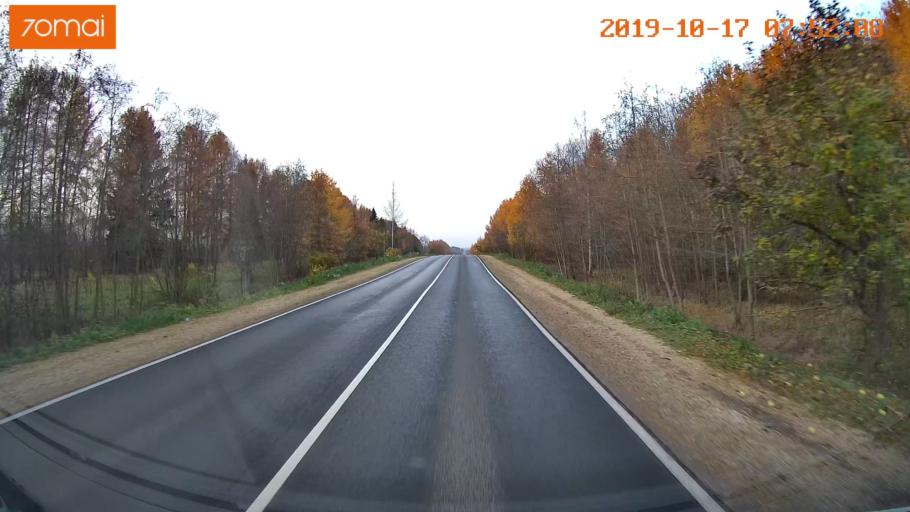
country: RU
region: Vladimir
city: Yur'yev-Pol'skiy
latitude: 56.4756
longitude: 39.6455
